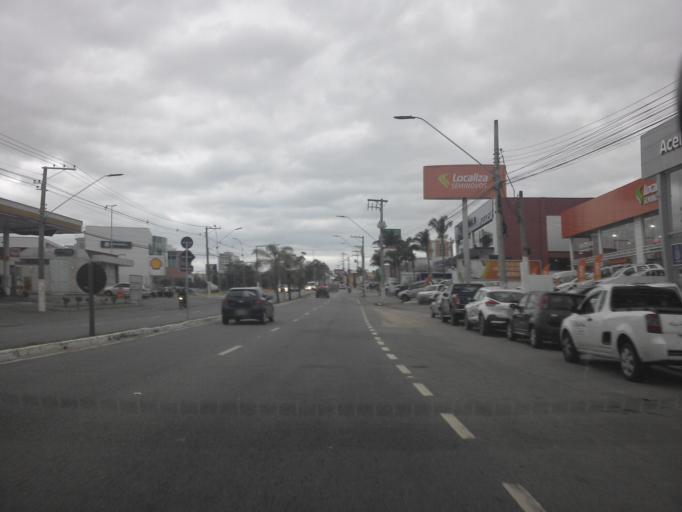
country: BR
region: Sao Paulo
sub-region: Taubate
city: Taubate
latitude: -23.0246
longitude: -45.5842
